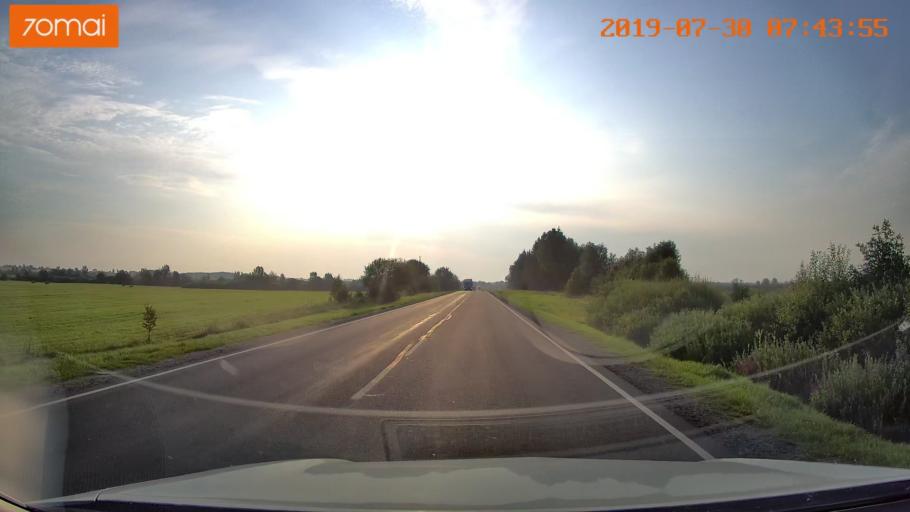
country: RU
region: Kaliningrad
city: Gvardeysk
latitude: 54.6494
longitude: 21.3138
